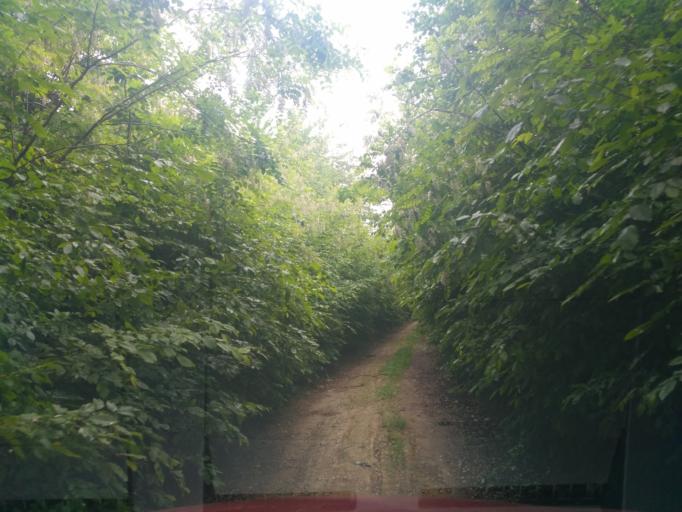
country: SK
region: Kosicky
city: Moldava nad Bodvou
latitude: 48.6938
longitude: 21.0764
